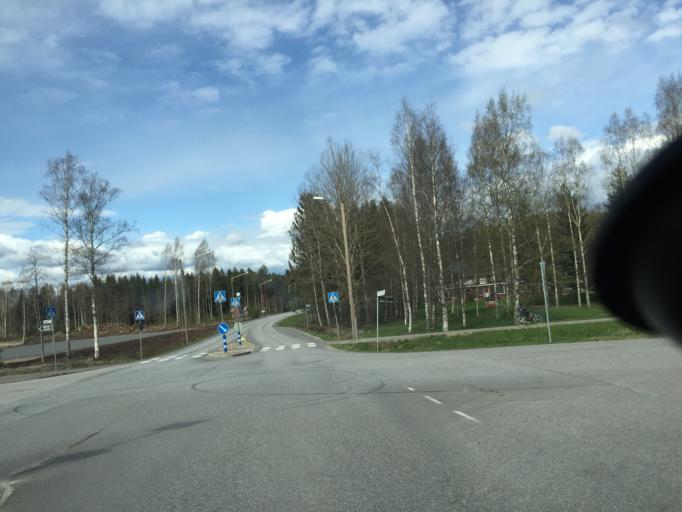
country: FI
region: Uusimaa
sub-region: Raaseporin
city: Ekenaes
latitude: 60.0582
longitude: 23.2981
